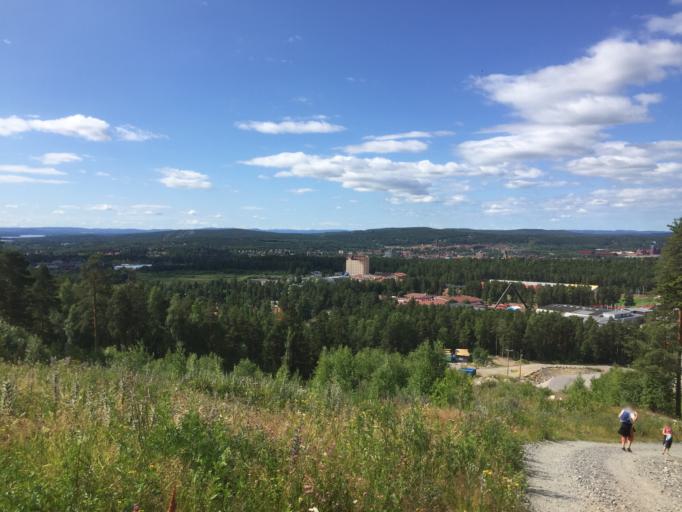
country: SE
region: Dalarna
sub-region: Faluns Kommun
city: Falun
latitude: 60.6203
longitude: 15.6644
